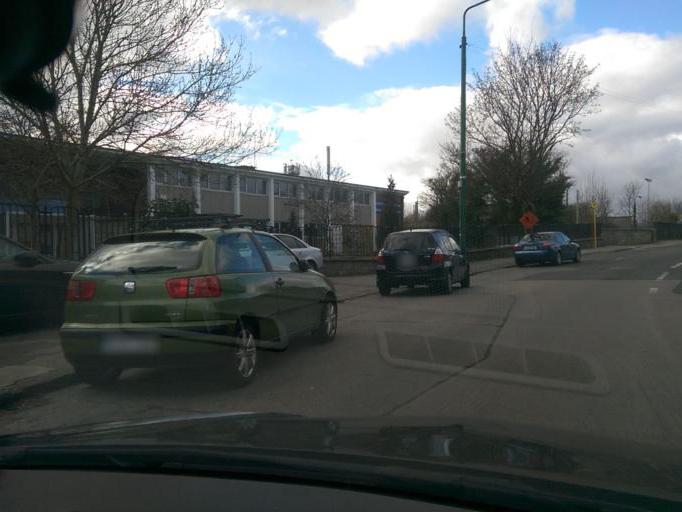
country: IE
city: Donnycarney
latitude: 53.3713
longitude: -6.2072
